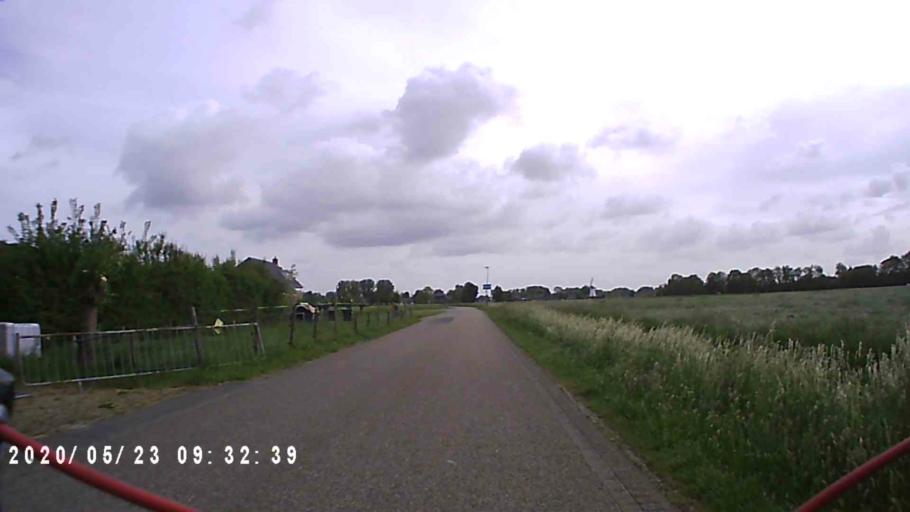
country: NL
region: Groningen
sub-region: Gemeente Slochteren
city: Slochteren
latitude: 53.2967
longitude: 6.7194
